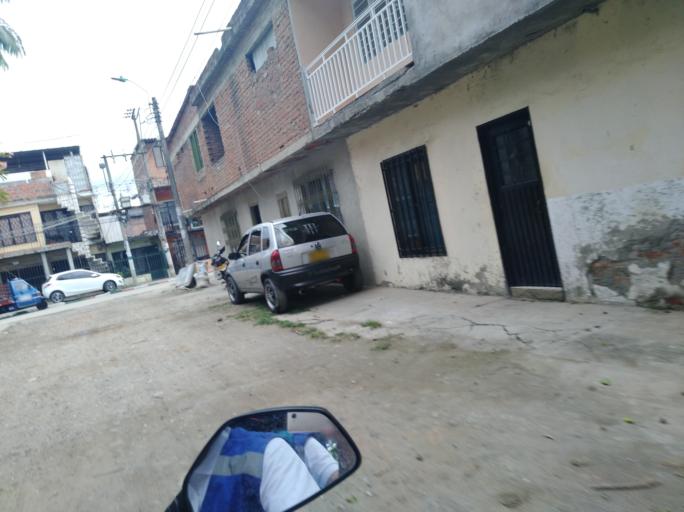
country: CO
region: Valle del Cauca
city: Cali
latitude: 3.4757
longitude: -76.4794
